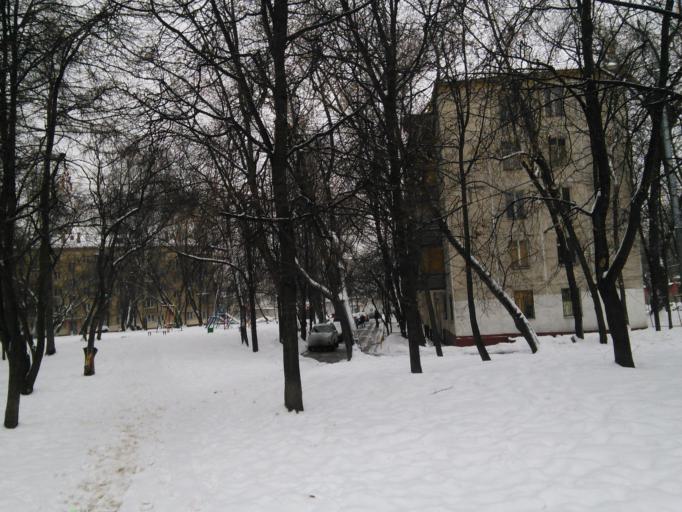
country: RU
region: Moscow
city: Lefortovo
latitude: 55.7673
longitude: 37.7108
